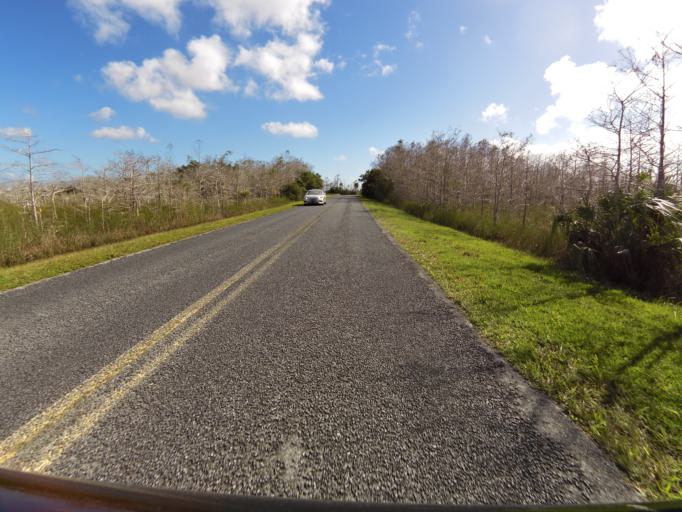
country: US
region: Florida
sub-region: Miami-Dade County
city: Florida City
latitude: 25.4288
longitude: -80.7718
